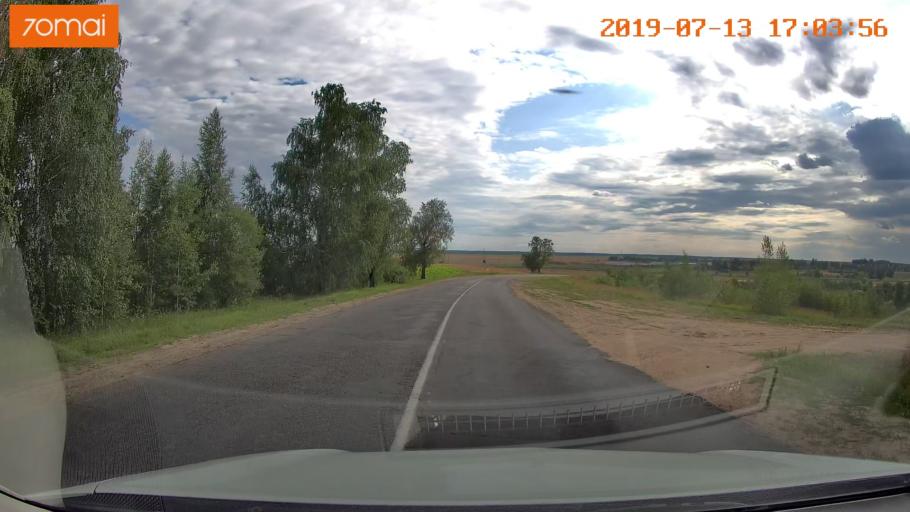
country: BY
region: Mogilev
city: Kirawsk
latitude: 53.2723
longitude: 29.3735
